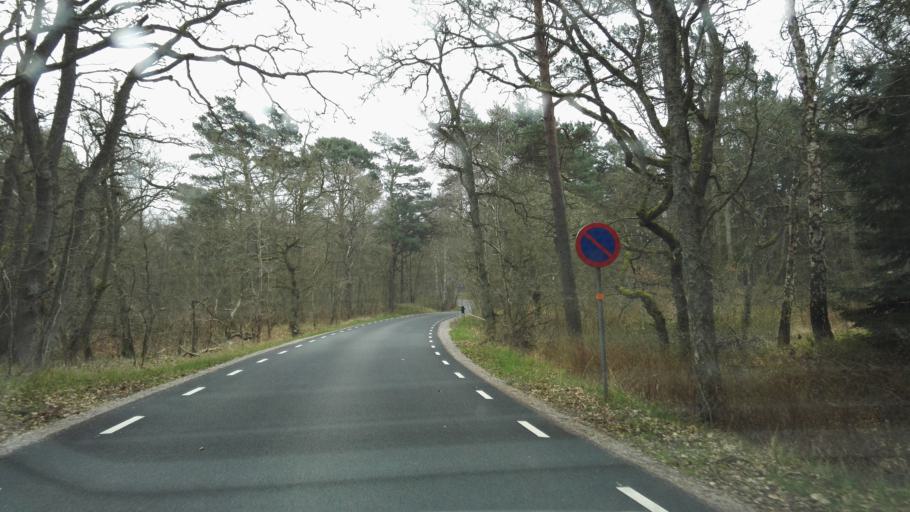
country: SE
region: Skane
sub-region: Simrishamns Kommun
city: Simrishamn
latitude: 55.3901
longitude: 14.1889
